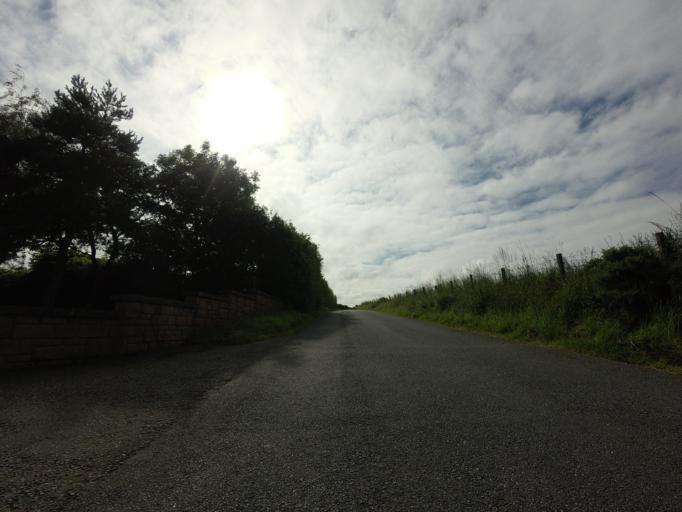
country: GB
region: Scotland
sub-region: Aberdeenshire
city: Turriff
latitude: 57.5336
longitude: -2.4197
